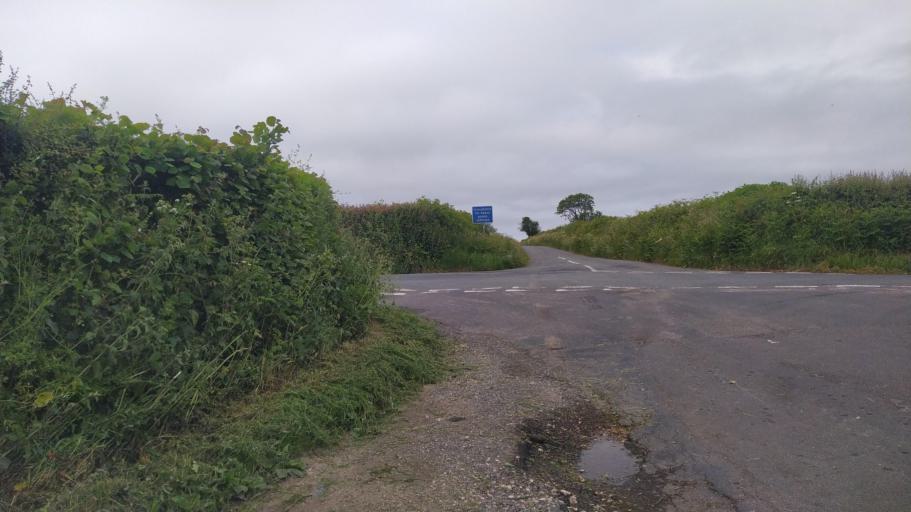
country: GB
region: England
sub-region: Somerset
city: Yeovil
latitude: 50.8351
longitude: -2.6075
